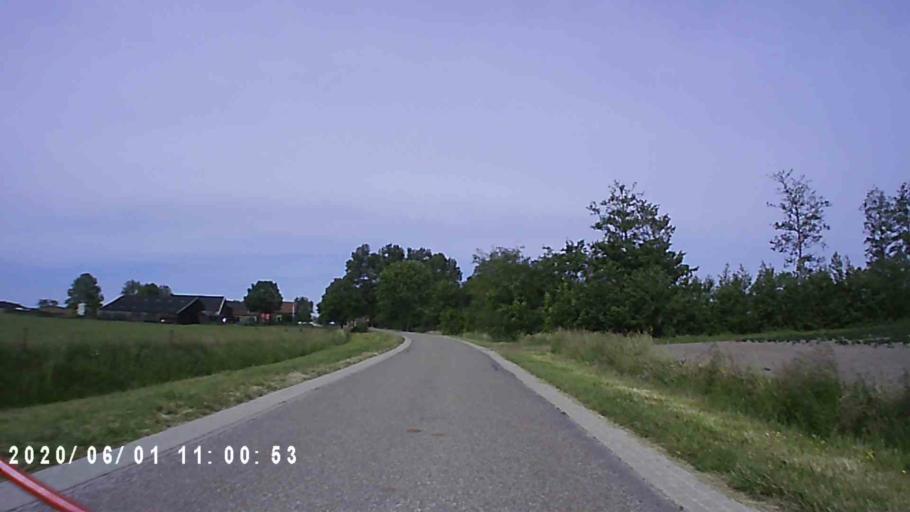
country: NL
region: Friesland
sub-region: Gemeente Franekeradeel
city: Sexbierum
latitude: 53.1969
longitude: 5.4834
